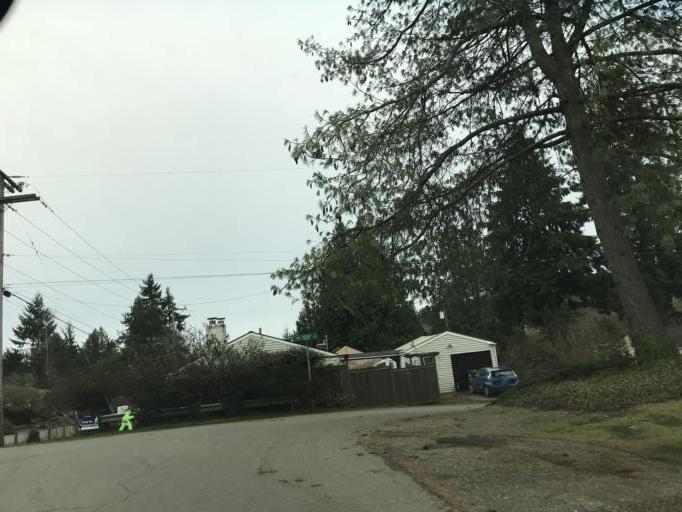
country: US
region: Washington
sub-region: King County
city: Lake Forest Park
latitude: 47.7050
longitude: -122.3073
